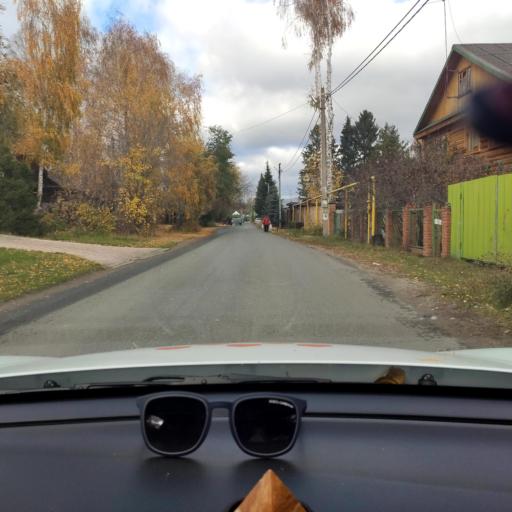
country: RU
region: Tatarstan
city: Verkhniy Uslon
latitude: 55.6196
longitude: 49.0144
